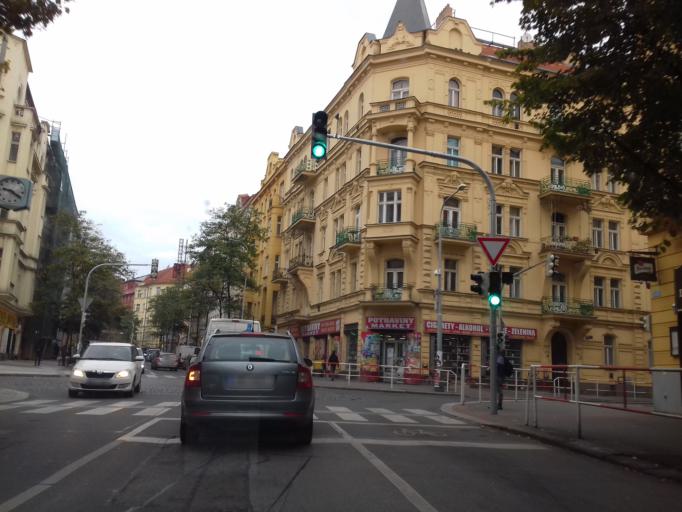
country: CZ
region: Praha
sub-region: Praha 8
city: Karlin
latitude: 50.0787
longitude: 14.4484
